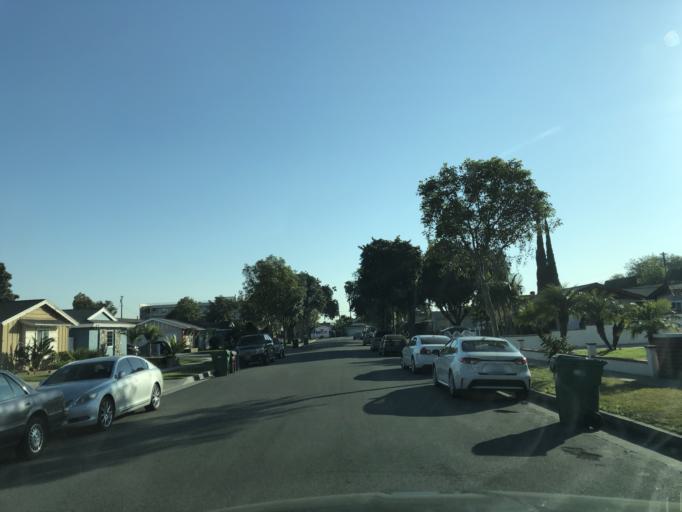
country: US
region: California
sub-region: Orange County
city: Santa Ana
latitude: 33.7647
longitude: -117.8554
